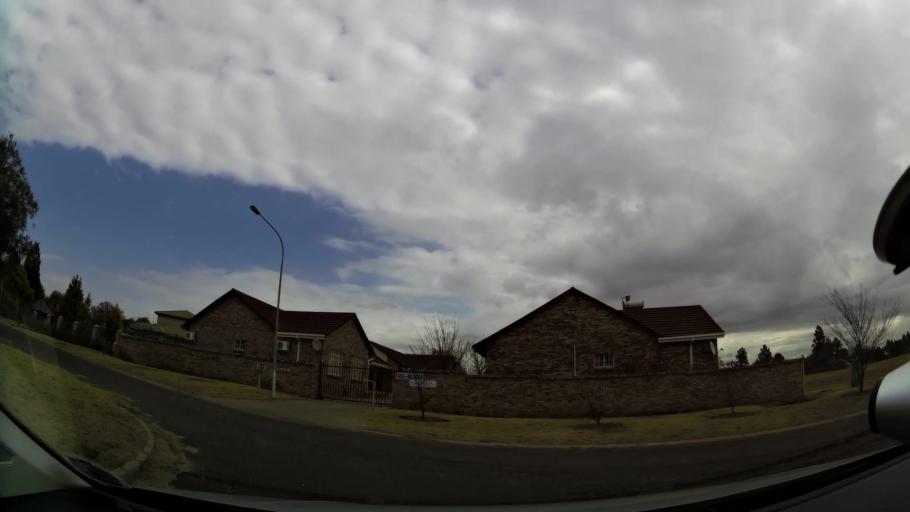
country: ZA
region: Orange Free State
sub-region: Fezile Dabi District Municipality
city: Kroonstad
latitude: -27.6305
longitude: 27.2435
